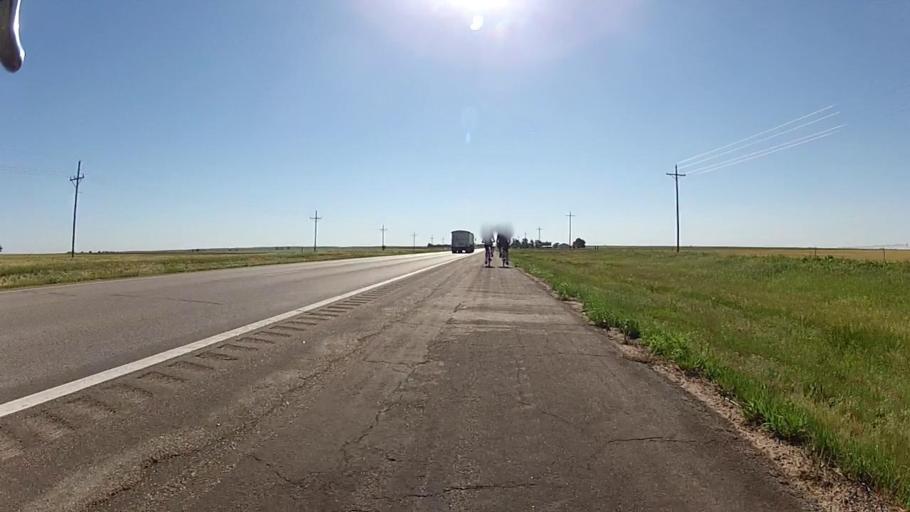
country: US
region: Kansas
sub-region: Kiowa County
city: Greensburg
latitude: 37.5863
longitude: -99.6044
